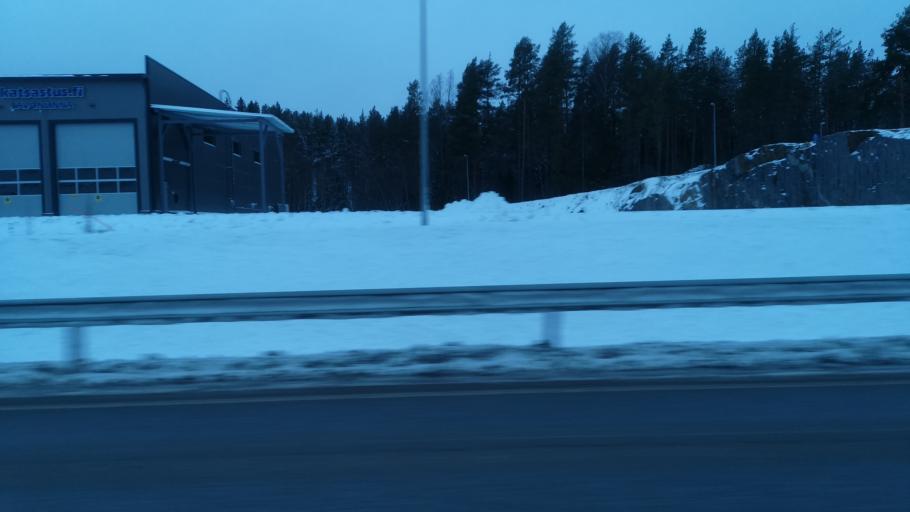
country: FI
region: Southern Savonia
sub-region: Savonlinna
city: Savonlinna
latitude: 61.8786
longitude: 28.8720
